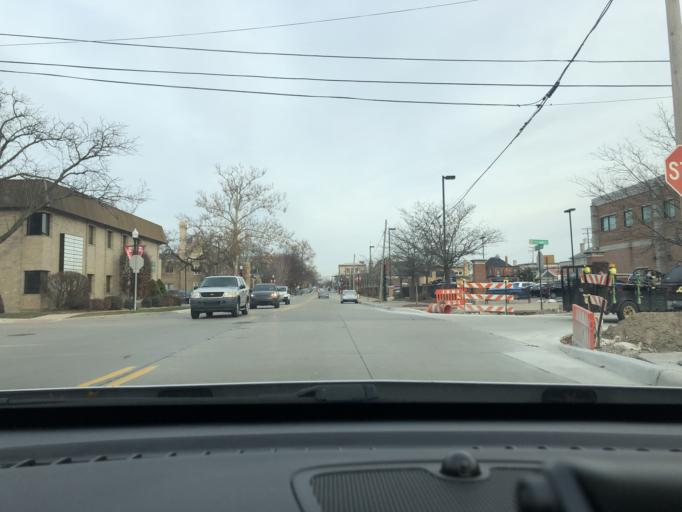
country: US
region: Michigan
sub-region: Wayne County
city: Dearborn Heights
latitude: 42.3063
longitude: -83.2486
